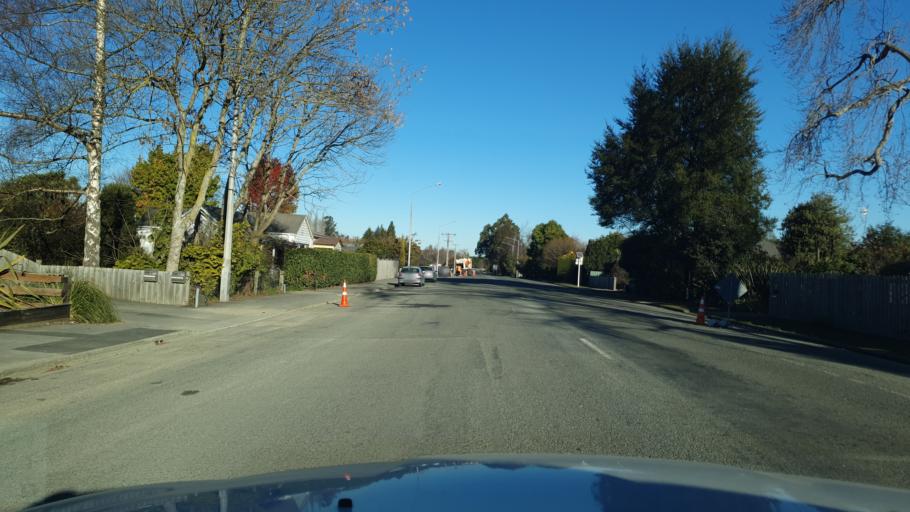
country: NZ
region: Canterbury
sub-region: Timaru District
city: Pleasant Point
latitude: -44.1087
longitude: 171.2451
